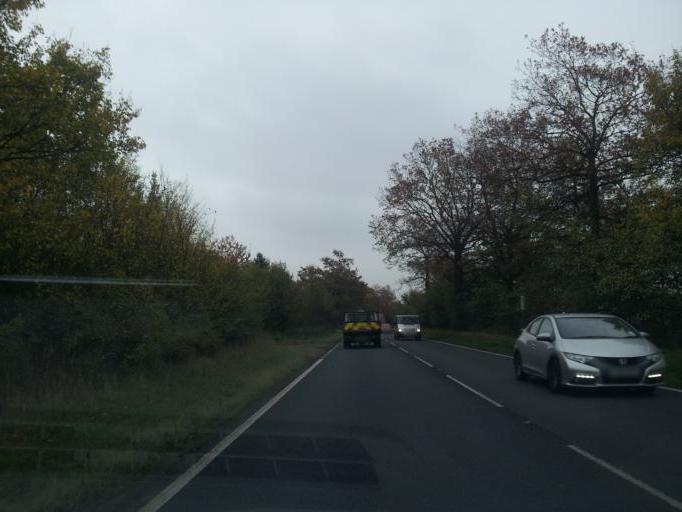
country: GB
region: England
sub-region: Cambridgeshire
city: Little Paxton
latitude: 52.2236
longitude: -0.2061
